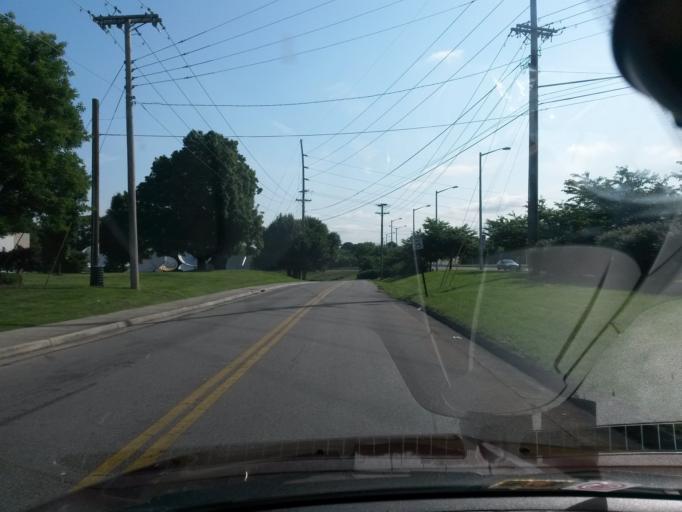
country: US
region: Virginia
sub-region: Roanoke County
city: Hollins
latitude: 37.3063
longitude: -79.9780
